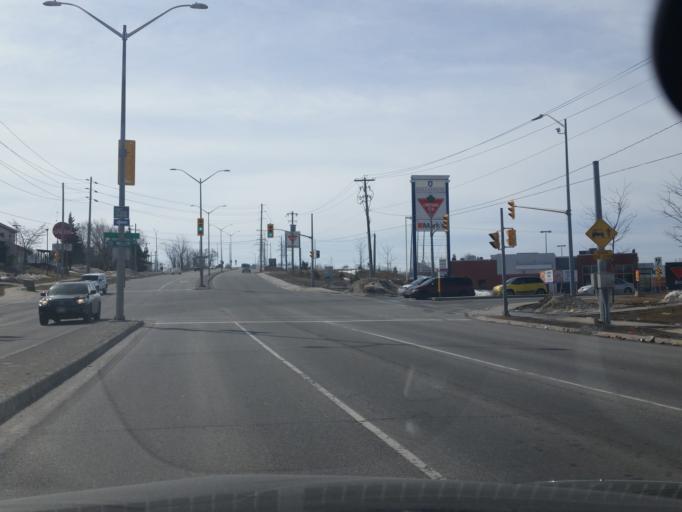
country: CA
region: Ontario
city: Kingston
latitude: 44.2643
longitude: -76.4984
